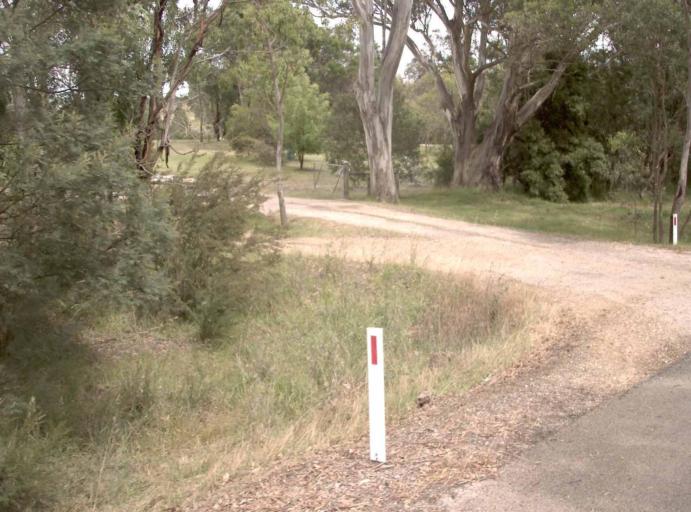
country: AU
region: Victoria
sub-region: Wellington
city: Sale
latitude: -37.9290
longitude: 147.0917
